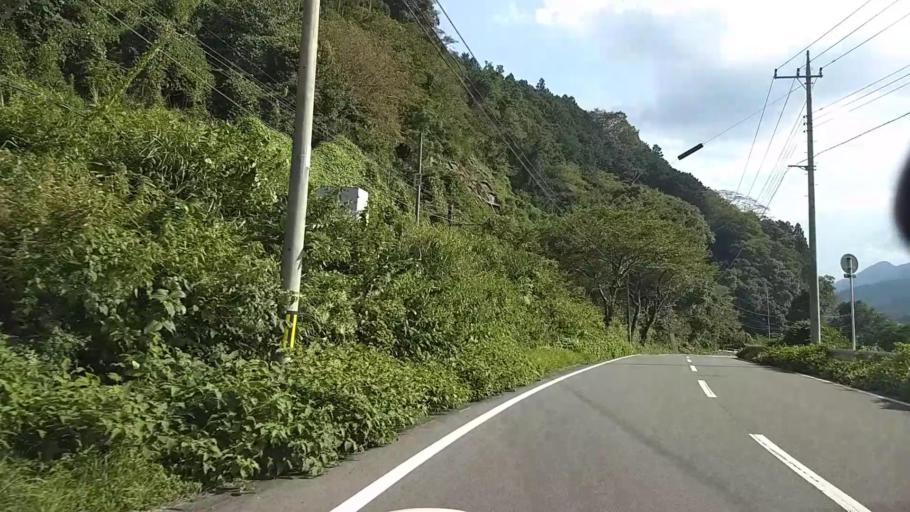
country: JP
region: Shizuoka
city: Fujinomiya
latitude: 35.2913
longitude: 138.4602
